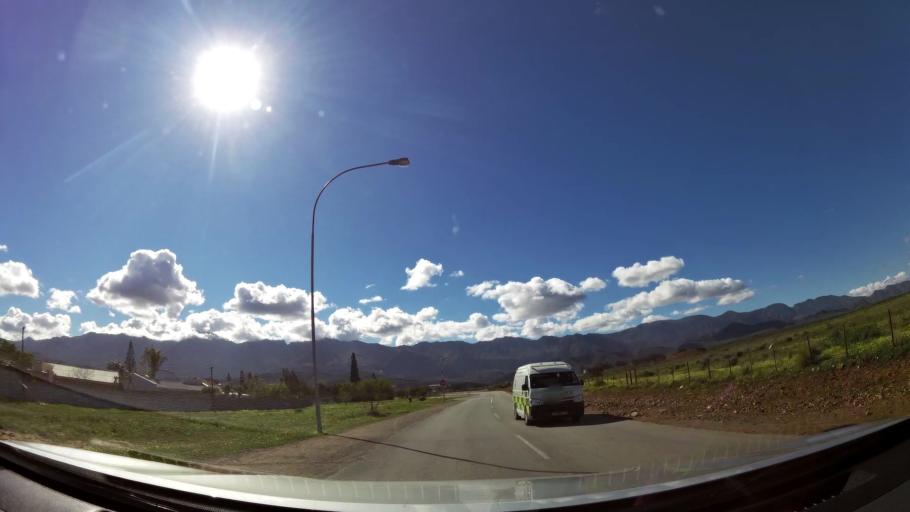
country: ZA
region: Western Cape
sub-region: Cape Winelands District Municipality
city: Ashton
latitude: -33.8107
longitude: 19.8979
